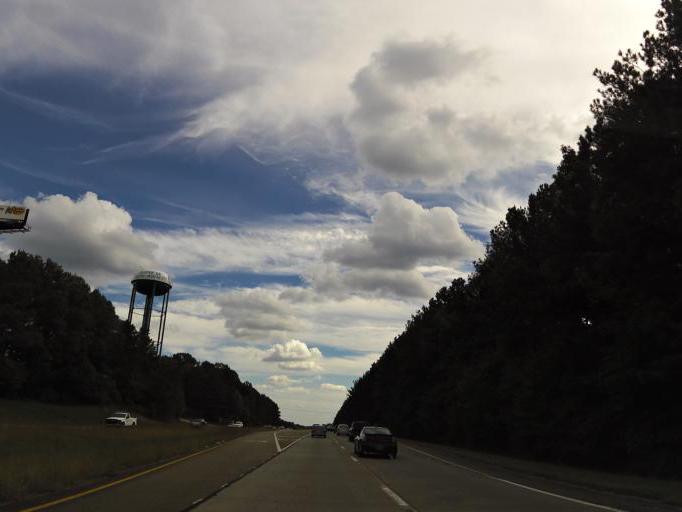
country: US
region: Georgia
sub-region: Pickens County
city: Jasper
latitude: 34.4267
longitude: -84.4328
